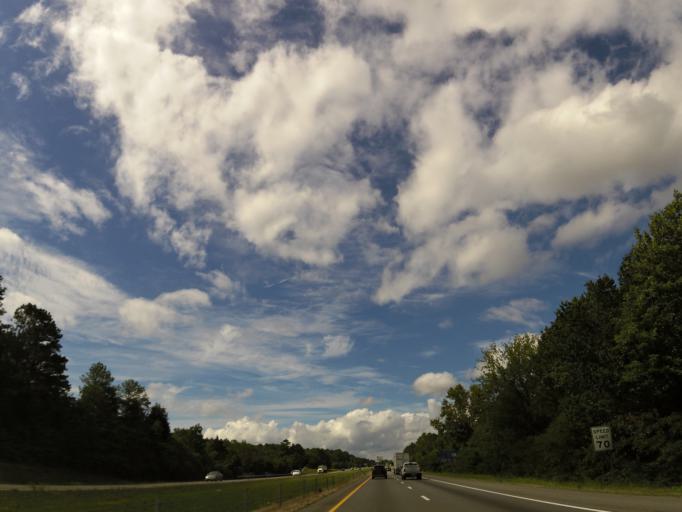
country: US
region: Tennessee
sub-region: Bradley County
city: Hopewell
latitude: 35.2054
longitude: -84.8721
